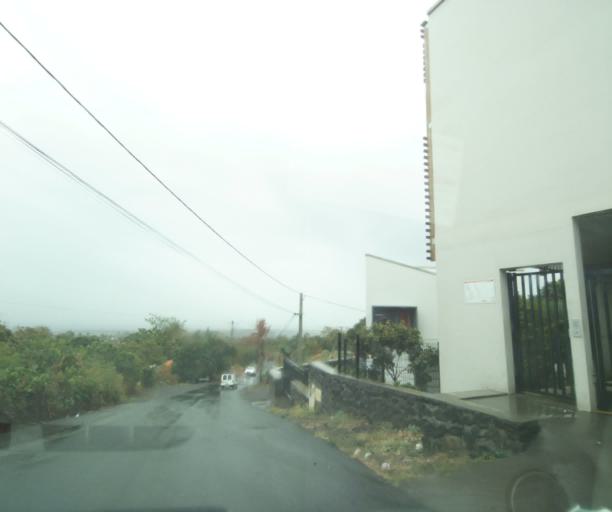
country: RE
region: Reunion
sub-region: Reunion
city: La Possession
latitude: -20.9772
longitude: 55.3347
